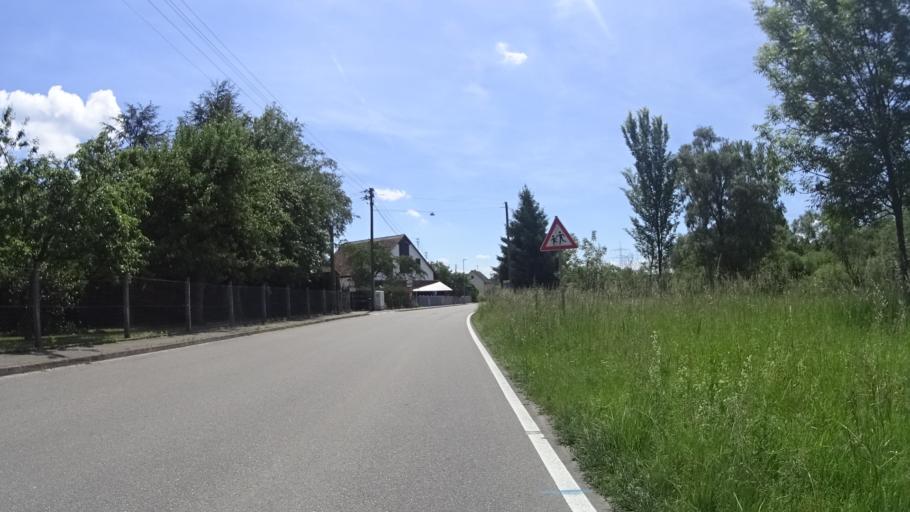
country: DE
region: Baden-Wuerttemberg
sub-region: Freiburg Region
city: Schwanau
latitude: 48.3324
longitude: 7.7524
